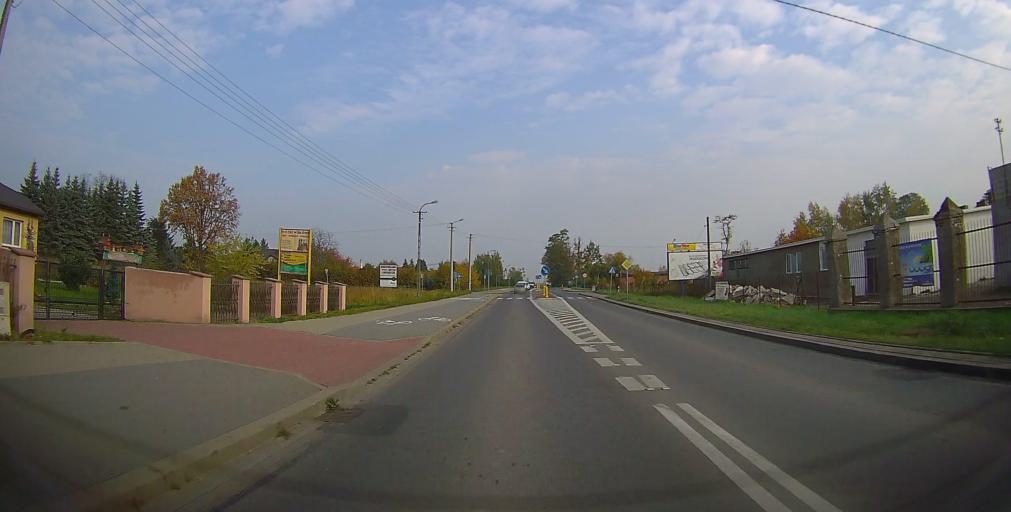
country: PL
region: Masovian Voivodeship
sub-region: Powiat grojecki
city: Mogielnica
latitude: 51.7060
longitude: 20.7376
